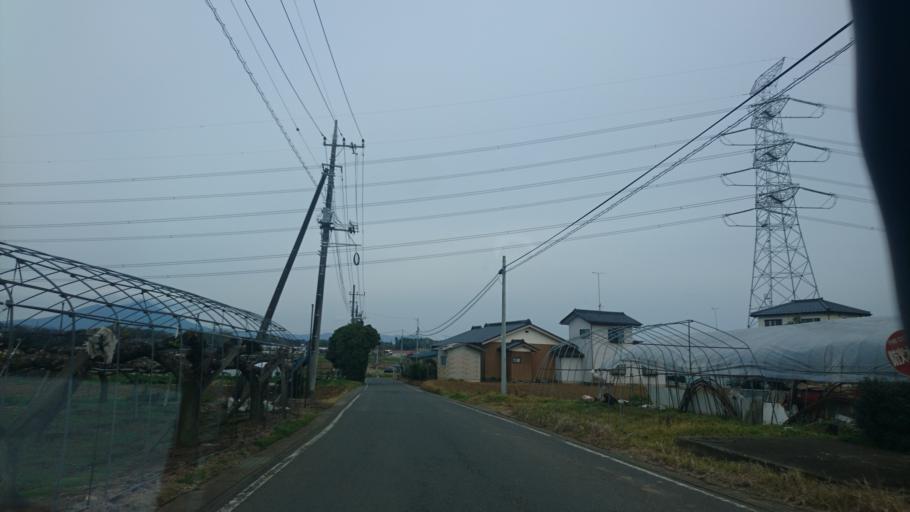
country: JP
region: Ibaraki
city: Shimodate
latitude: 36.2171
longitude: 139.9609
